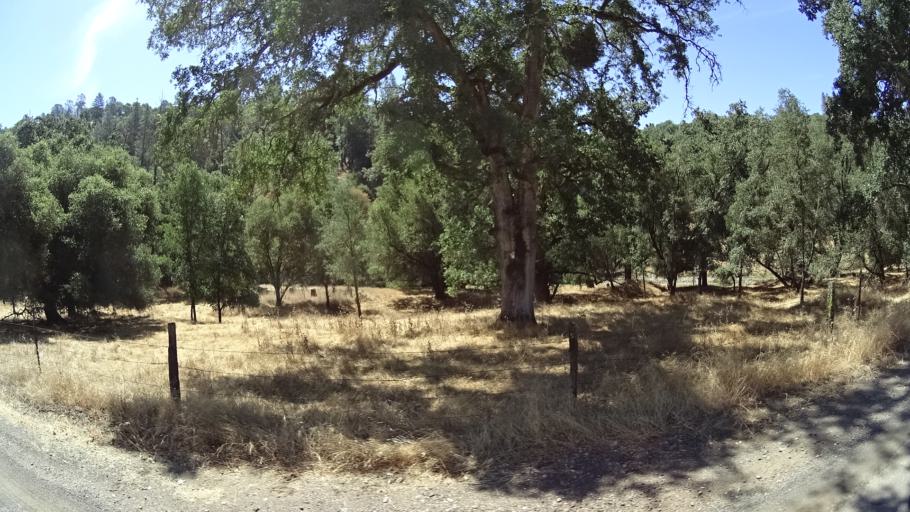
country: US
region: California
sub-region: Calaveras County
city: Angels Camp
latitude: 38.1339
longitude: -120.5629
